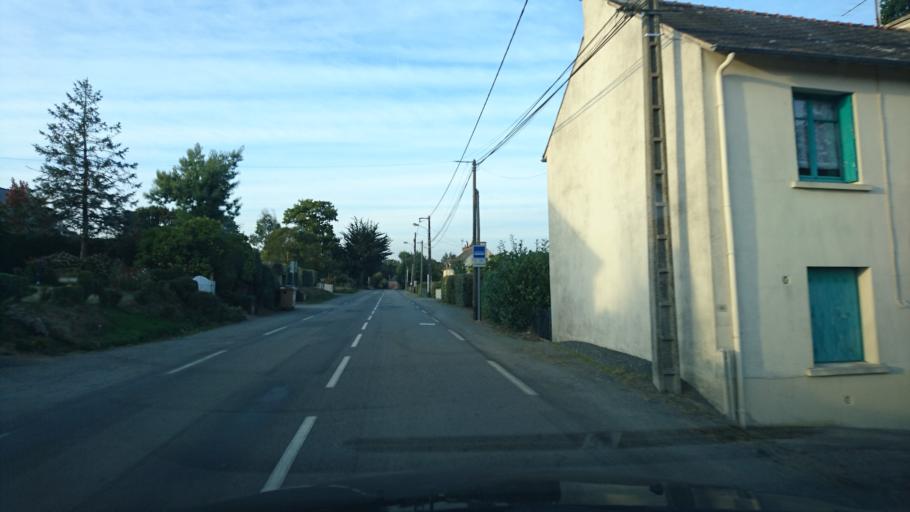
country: FR
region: Brittany
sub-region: Departement d'Ille-et-Vilaine
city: Bains-sur-Oust
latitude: 47.7357
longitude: -2.0498
